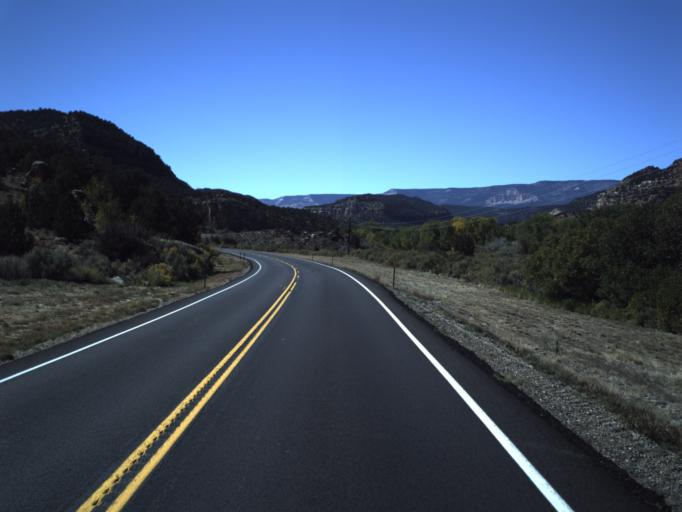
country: US
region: Utah
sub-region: Wayne County
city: Loa
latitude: 37.7683
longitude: -111.6694
